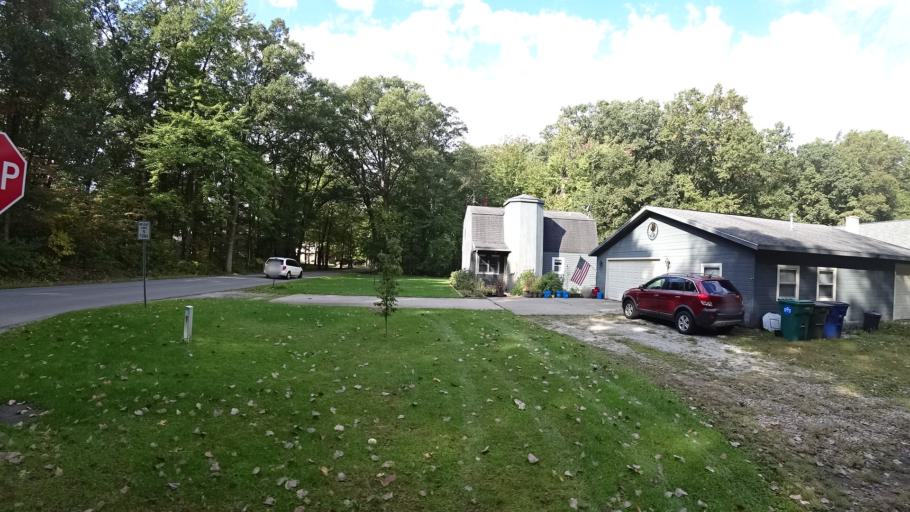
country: US
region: Indiana
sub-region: LaPorte County
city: Trail Creek
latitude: 41.6913
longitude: -86.8715
